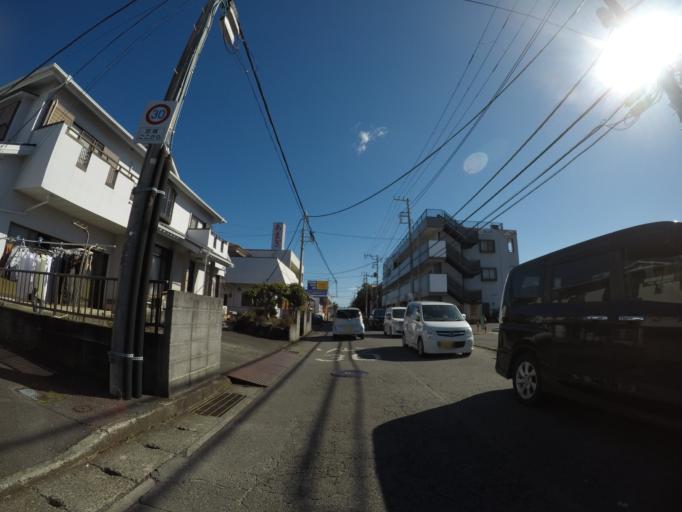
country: JP
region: Shizuoka
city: Numazu
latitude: 35.1305
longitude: 138.8019
